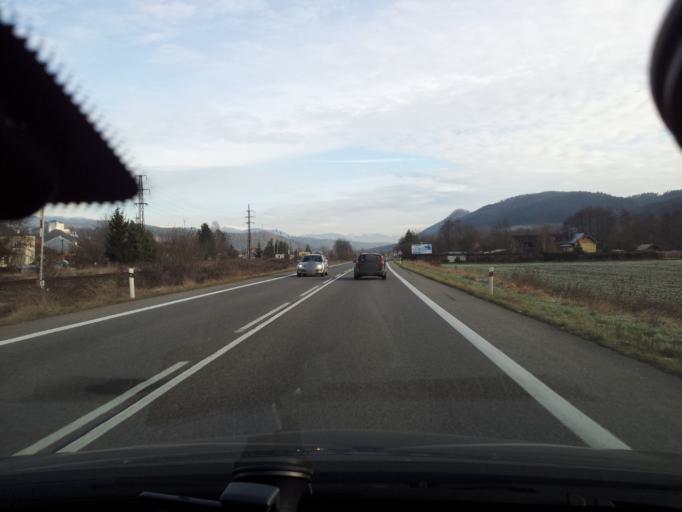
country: SK
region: Banskobystricky
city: Hrochot,Slovakia
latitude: 48.7598
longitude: 19.2699
